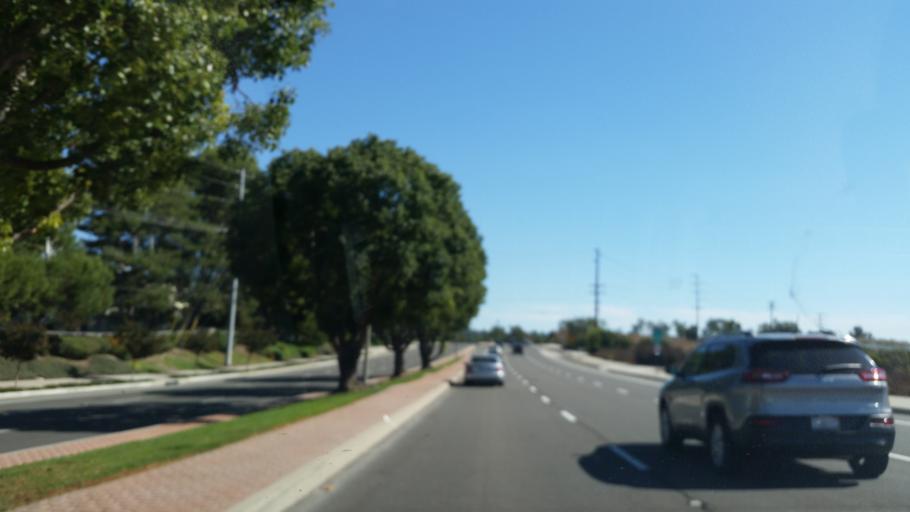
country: US
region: California
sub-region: Orange County
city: Laguna Hills
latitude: 33.5890
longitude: -117.7115
